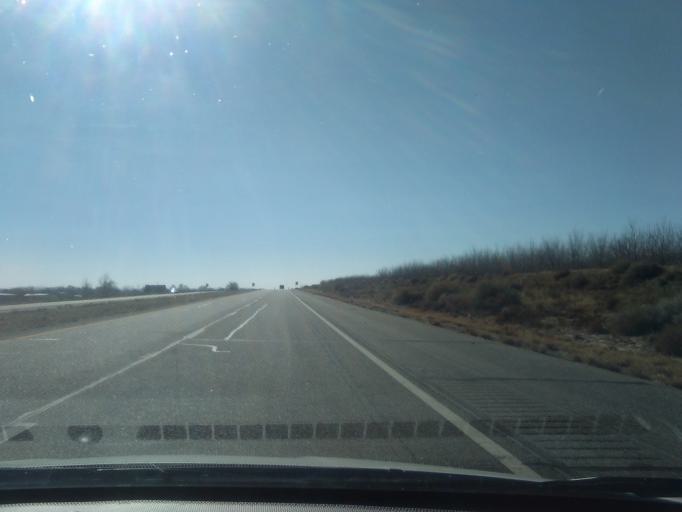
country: US
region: New Mexico
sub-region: Valencia County
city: Jarales
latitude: 34.5813
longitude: -106.7916
